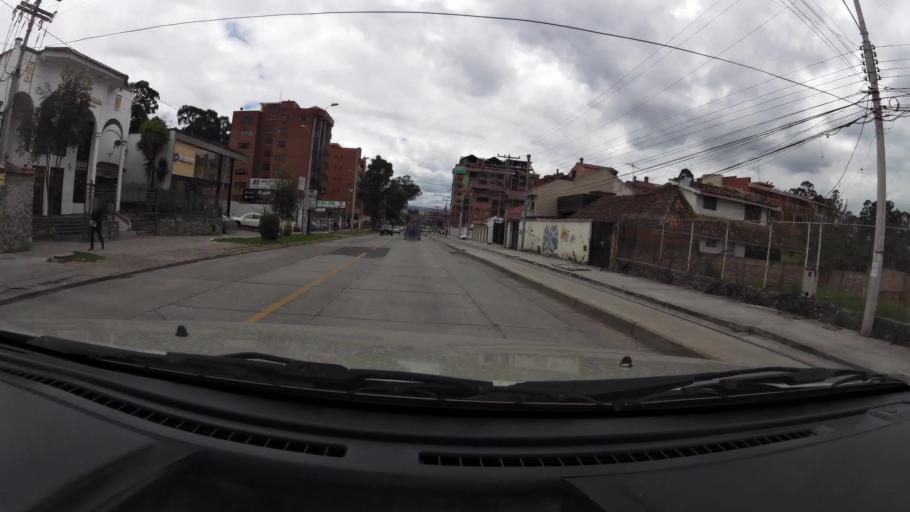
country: EC
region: Azuay
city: Cuenca
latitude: -2.8913
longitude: -79.0227
